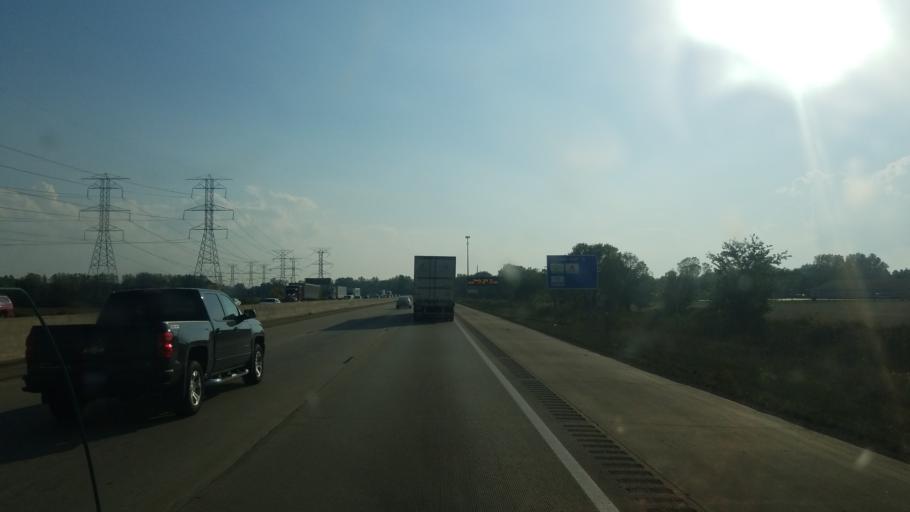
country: US
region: Michigan
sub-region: Monroe County
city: Detroit Beach
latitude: 41.9548
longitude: -83.3587
